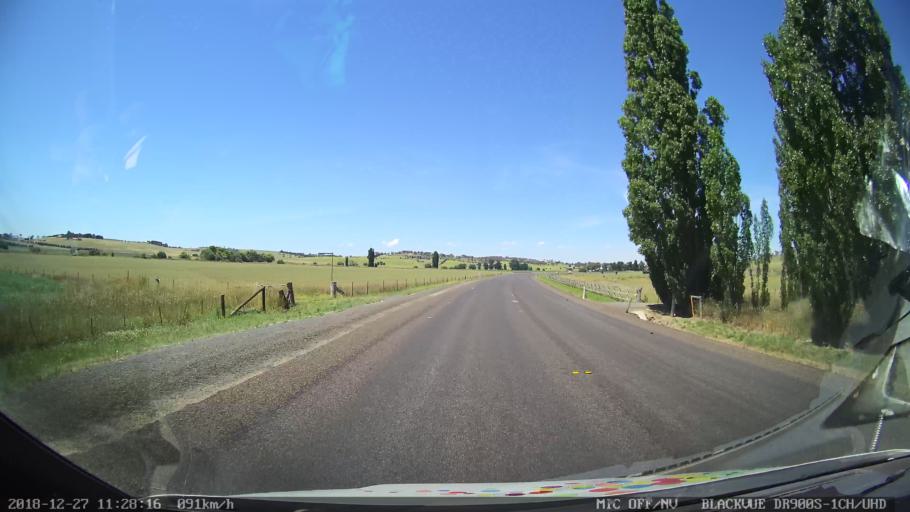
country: AU
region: New South Wales
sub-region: Bathurst Regional
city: Perthville
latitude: -33.4737
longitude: 149.5646
